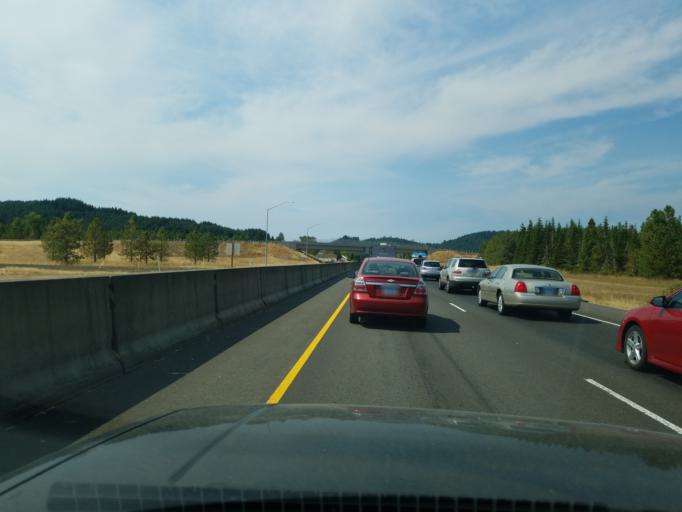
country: US
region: Oregon
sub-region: Yamhill County
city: Willamina
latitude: 45.0535
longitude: -123.5393
